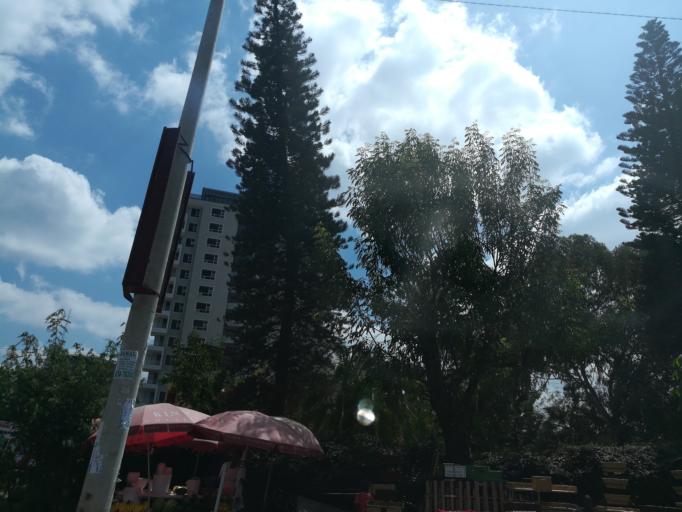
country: KE
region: Nairobi Area
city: Nairobi
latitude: -1.2927
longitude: 36.7905
